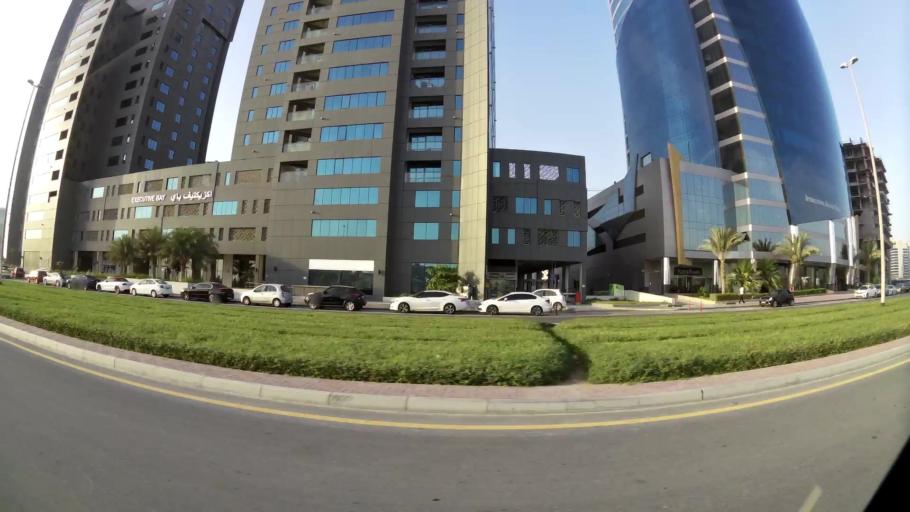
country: AE
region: Dubai
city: Dubai
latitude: 25.1778
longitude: 55.2668
